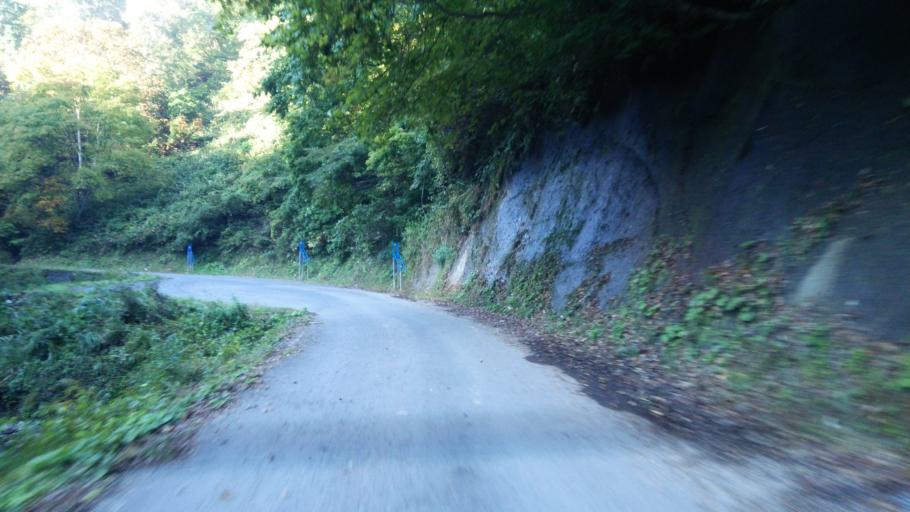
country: JP
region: Fukushima
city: Kitakata
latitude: 37.4060
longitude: 139.7311
